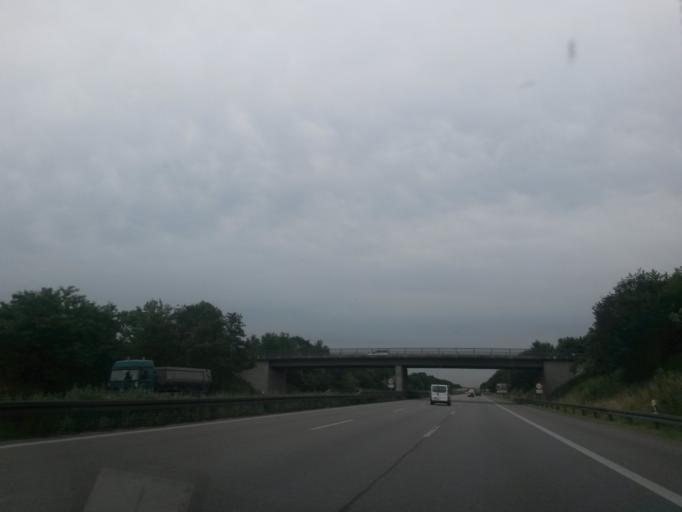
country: DE
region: Bavaria
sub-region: Upper Bavaria
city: Manching
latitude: 48.7374
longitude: 11.4671
